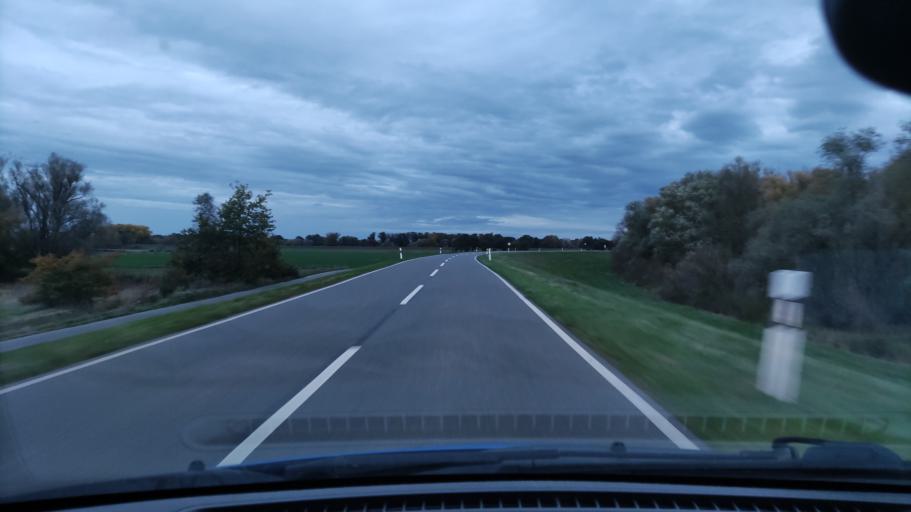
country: DE
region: Lower Saxony
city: Gorleben
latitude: 53.0533
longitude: 11.3898
